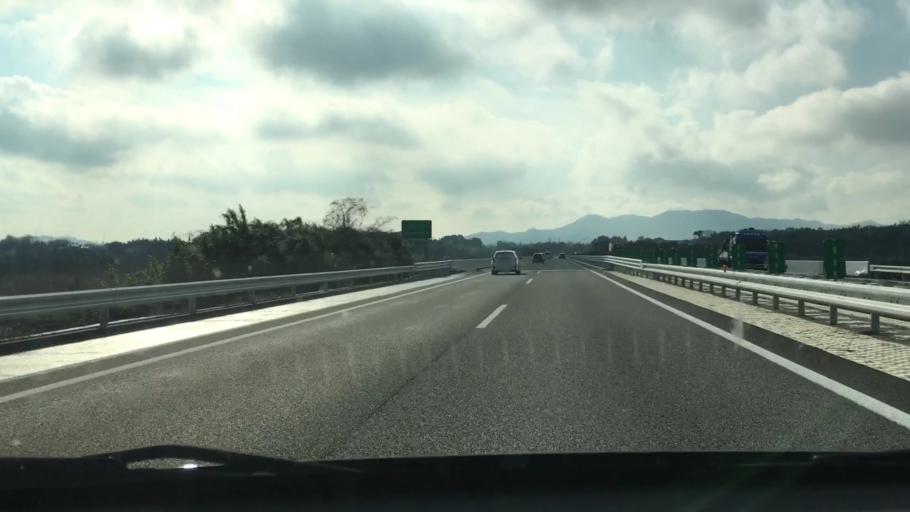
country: JP
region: Kumamoto
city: Uto
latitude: 32.7132
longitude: 130.7642
